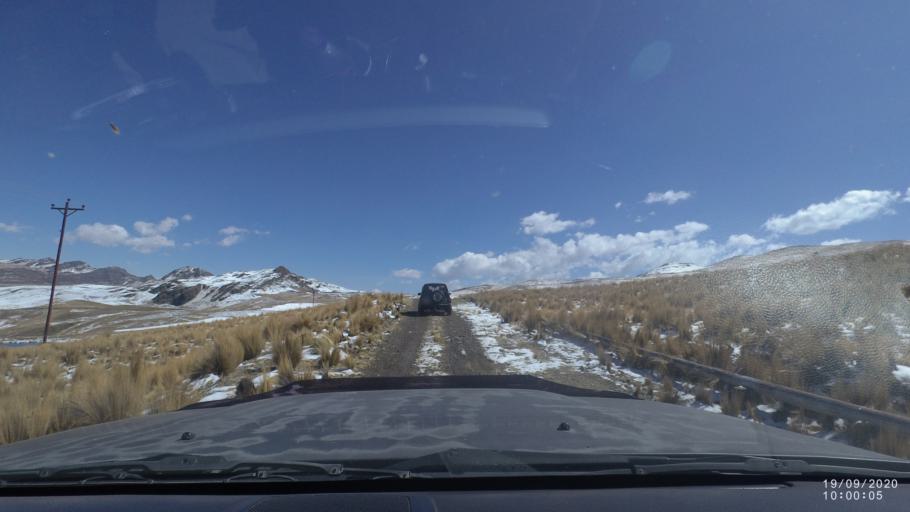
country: BO
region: Cochabamba
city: Cochabamba
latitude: -17.3057
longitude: -66.0889
